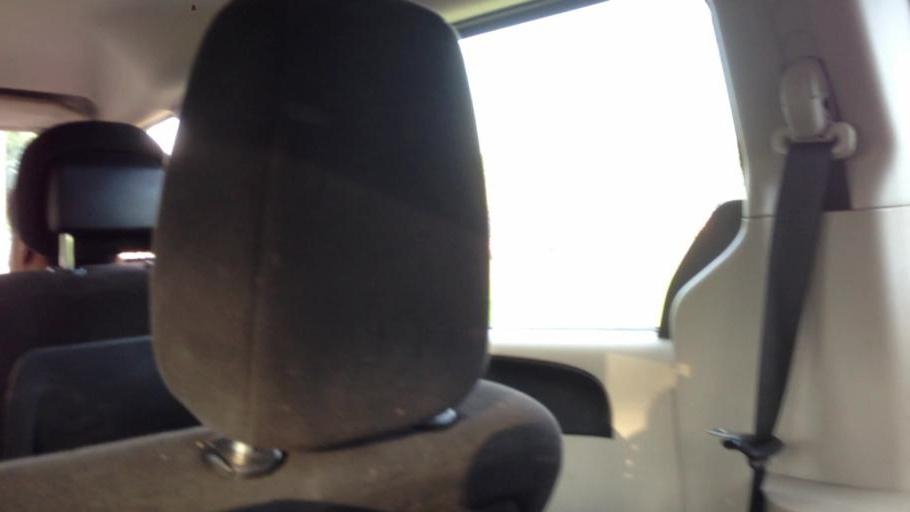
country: US
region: New York
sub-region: Dutchess County
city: Rhinebeck
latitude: 41.9399
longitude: -73.9073
